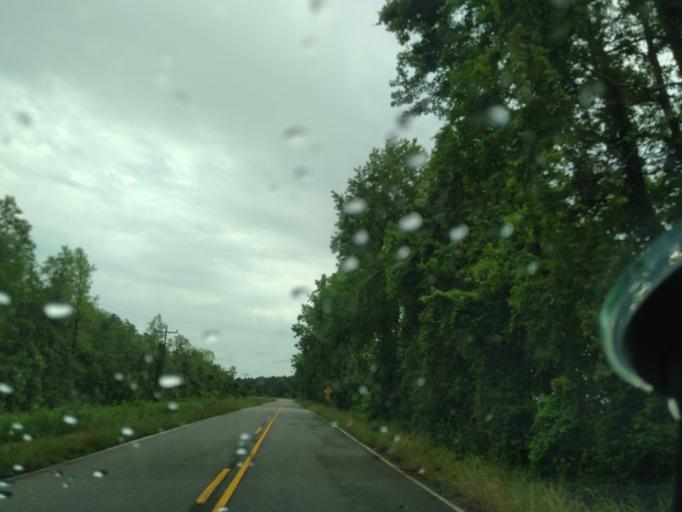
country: US
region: North Carolina
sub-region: Washington County
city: Plymouth
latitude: 35.7711
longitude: -76.5271
